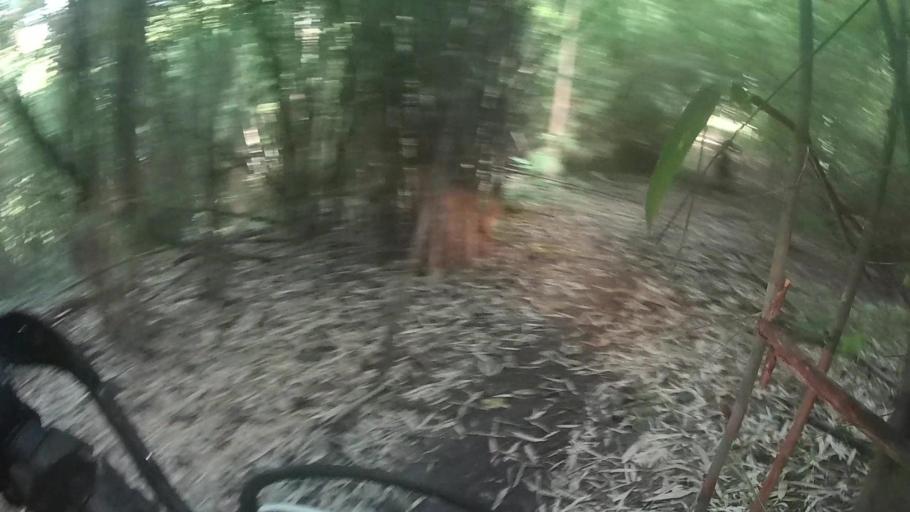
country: TH
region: Chiang Mai
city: Mae Taeng
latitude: 18.9909
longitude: 98.8581
